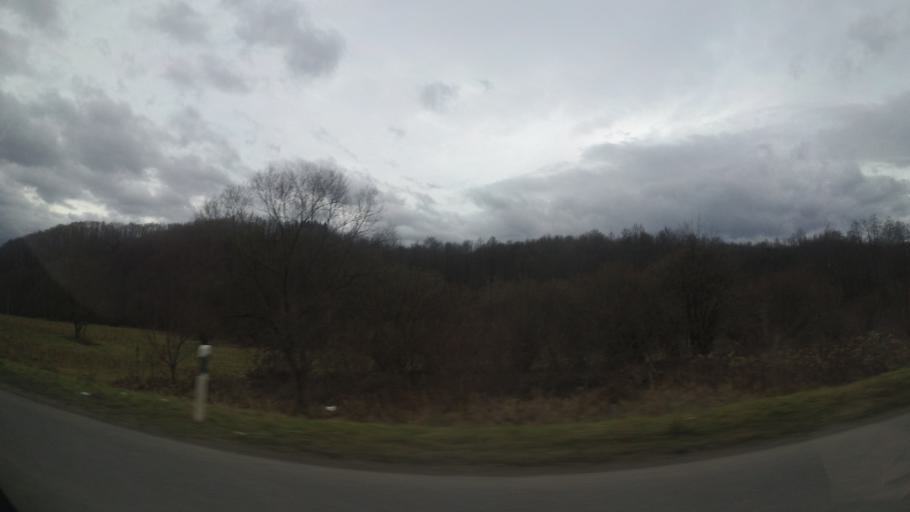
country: HR
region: Karlovacka
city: Vojnic
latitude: 45.3285
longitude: 15.6221
